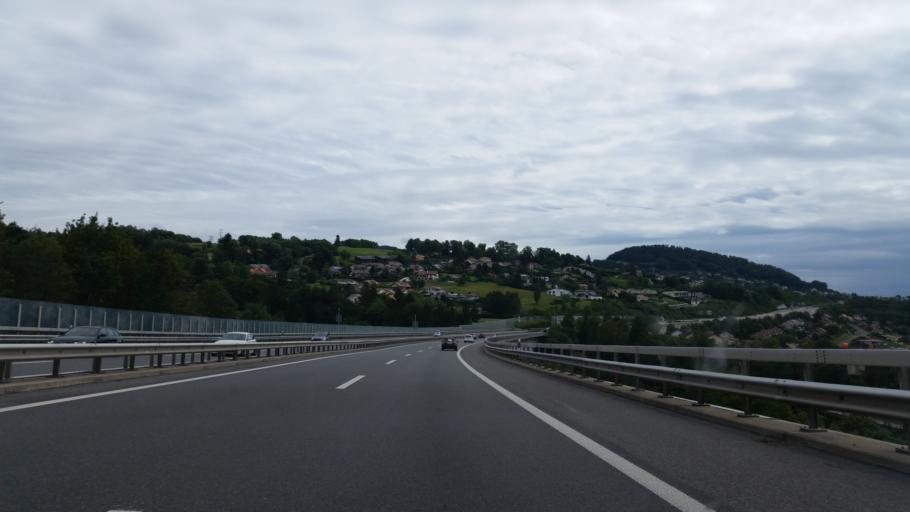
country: CH
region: Vaud
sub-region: Lavaux-Oron District
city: Lutry
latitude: 46.5166
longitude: 6.6936
